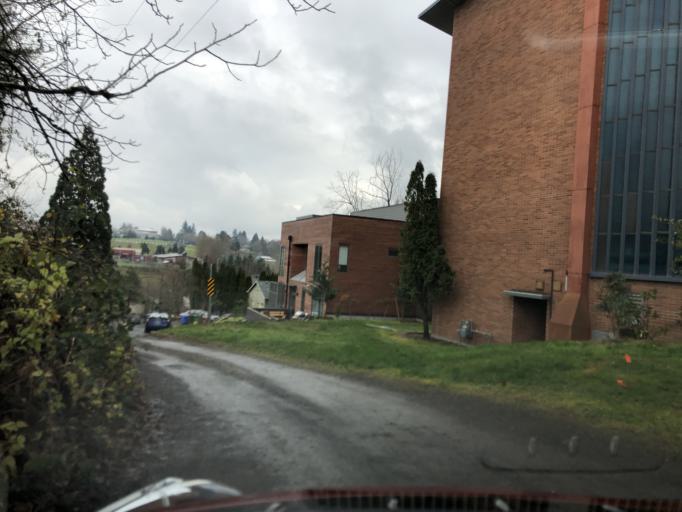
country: US
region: Oregon
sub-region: Multnomah County
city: Portland
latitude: 45.4768
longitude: -122.6998
